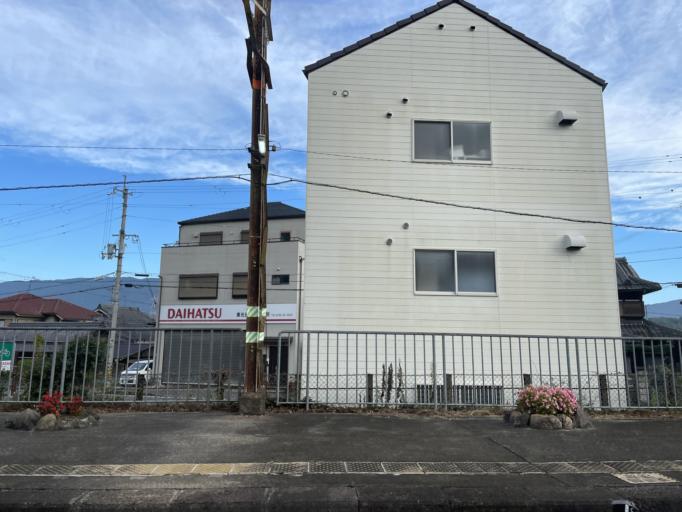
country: JP
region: Wakayama
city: Hashimoto
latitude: 34.3076
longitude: 135.6049
